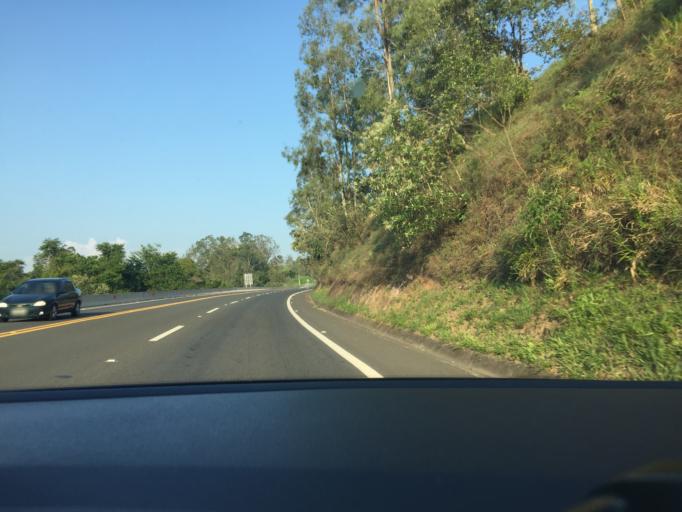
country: BR
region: Sao Paulo
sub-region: Louveira
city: Louveira
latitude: -23.0827
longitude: -46.9225
